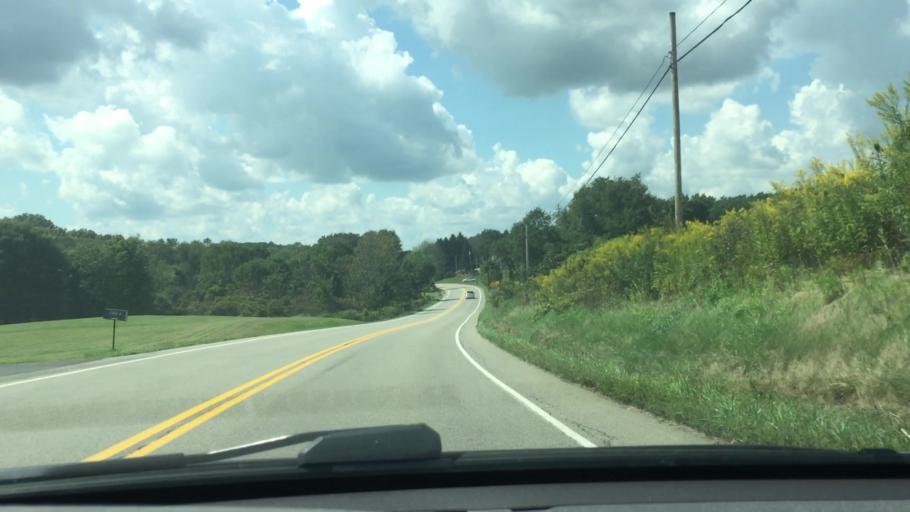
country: US
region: Pennsylvania
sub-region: Mercer County
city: Mercer
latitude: 41.1405
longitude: -80.2065
